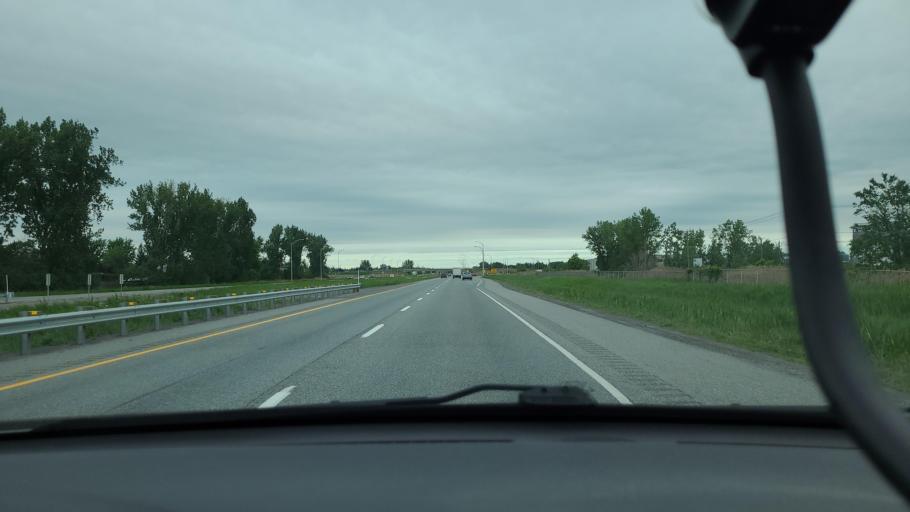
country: CA
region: Quebec
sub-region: Lanaudiere
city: Mascouche
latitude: 45.7356
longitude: -73.5998
